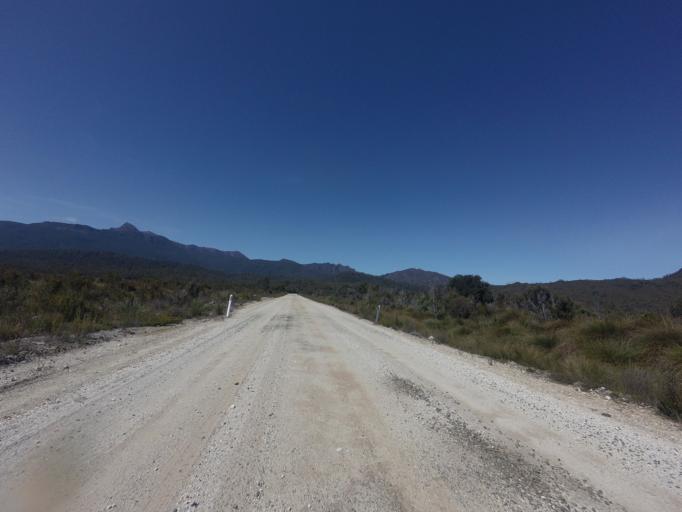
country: AU
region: Tasmania
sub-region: Huon Valley
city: Geeveston
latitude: -42.8959
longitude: 146.3739
